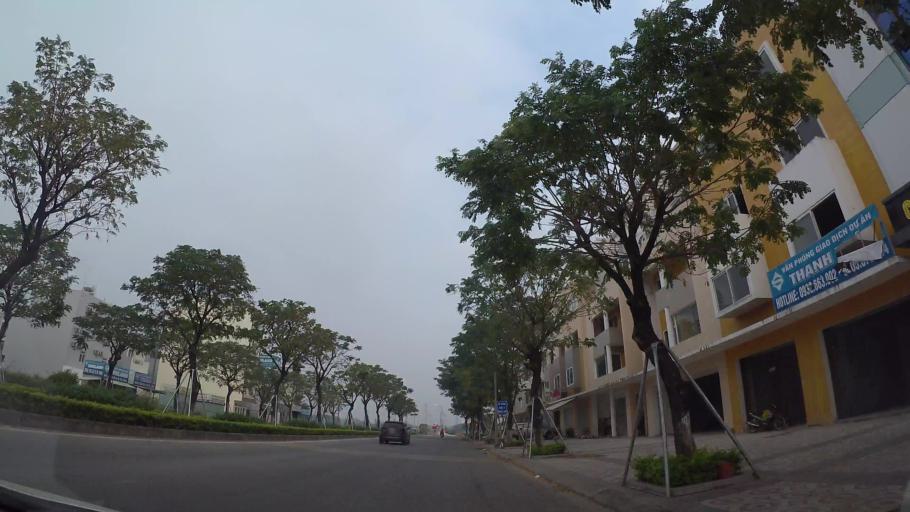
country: VN
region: Da Nang
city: Cam Le
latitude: 16.0220
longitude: 108.2257
